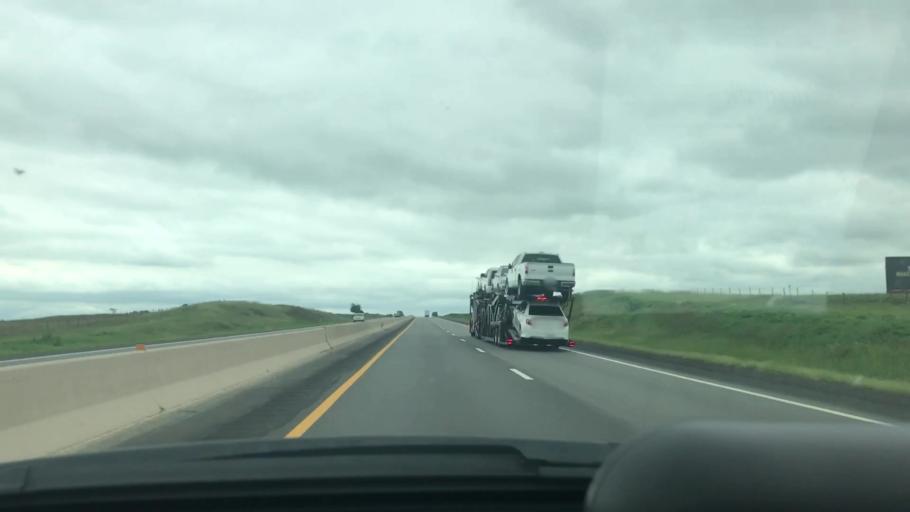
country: US
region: Oklahoma
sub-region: Ottawa County
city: Afton
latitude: 36.6938
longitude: -95.0104
